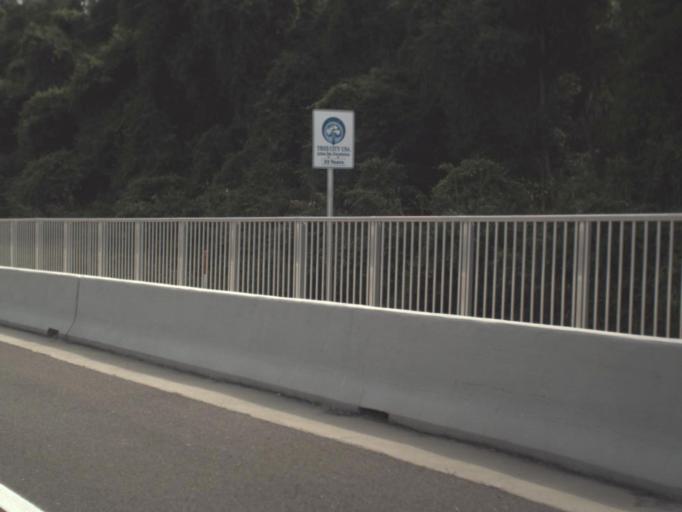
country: US
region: Florida
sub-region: Clay County
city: Orange Park
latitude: 30.1520
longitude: -81.7006
